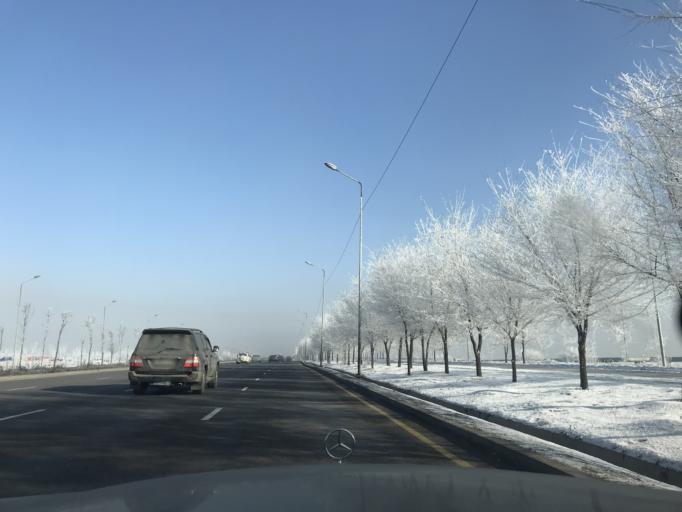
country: KZ
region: Almaty Oblysy
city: Burunday
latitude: 43.2917
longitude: 76.8295
